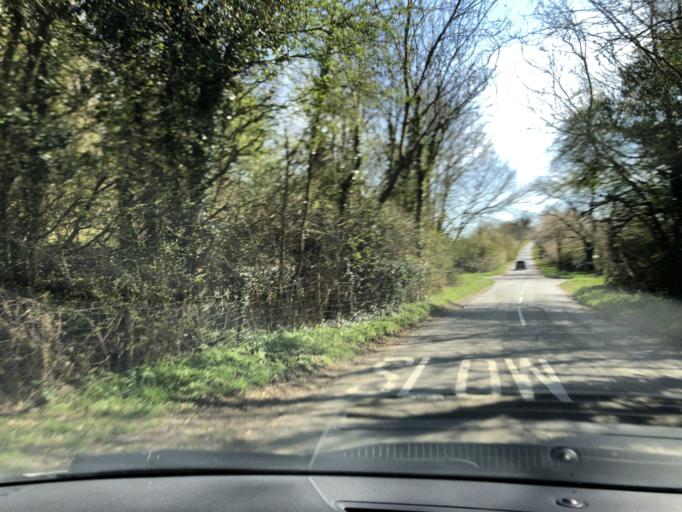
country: GB
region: England
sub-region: Oxfordshire
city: Hook Norton
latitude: 52.0045
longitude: -1.4398
